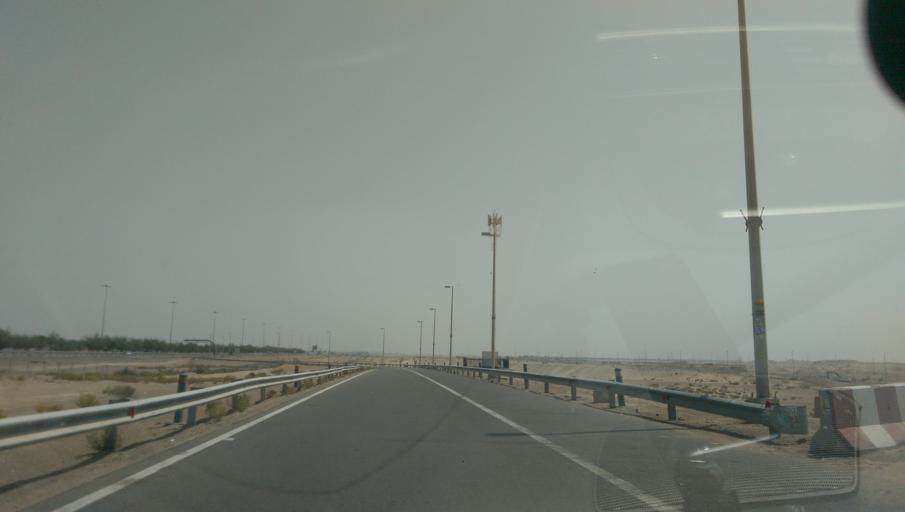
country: AE
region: Abu Dhabi
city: Abu Dhabi
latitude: 24.3874
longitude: 54.6642
